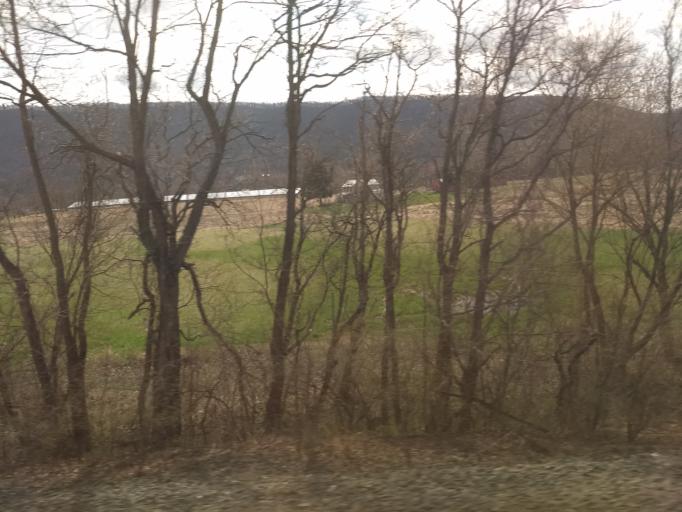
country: US
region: Pennsylvania
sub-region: Mifflin County
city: Lewistown
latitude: 40.5578
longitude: -77.6085
